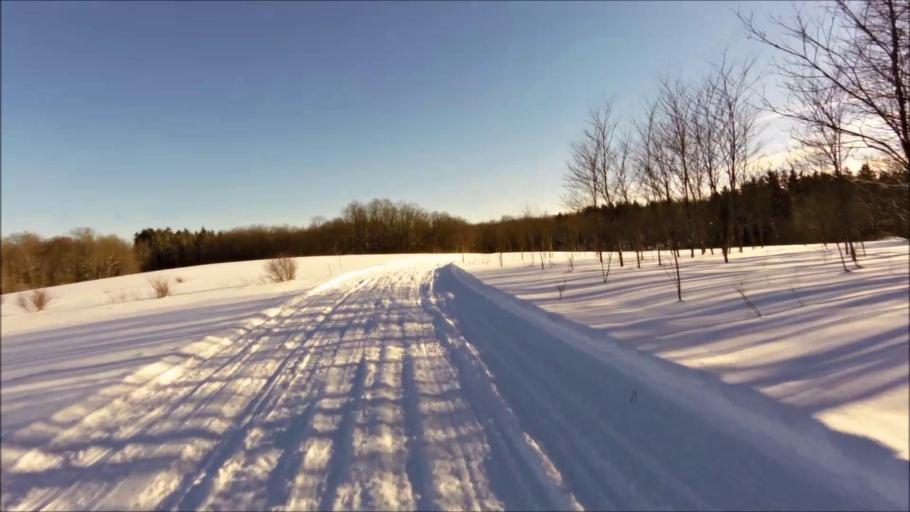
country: US
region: New York
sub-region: Chautauqua County
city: Mayville
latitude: 42.2517
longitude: -79.3860
